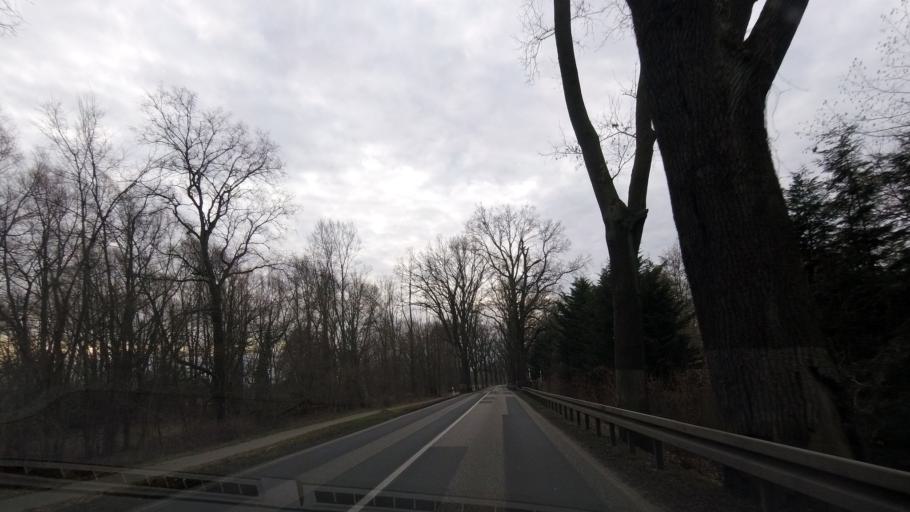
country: DE
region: Brandenburg
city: Erkner
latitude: 52.4006
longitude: 13.7471
